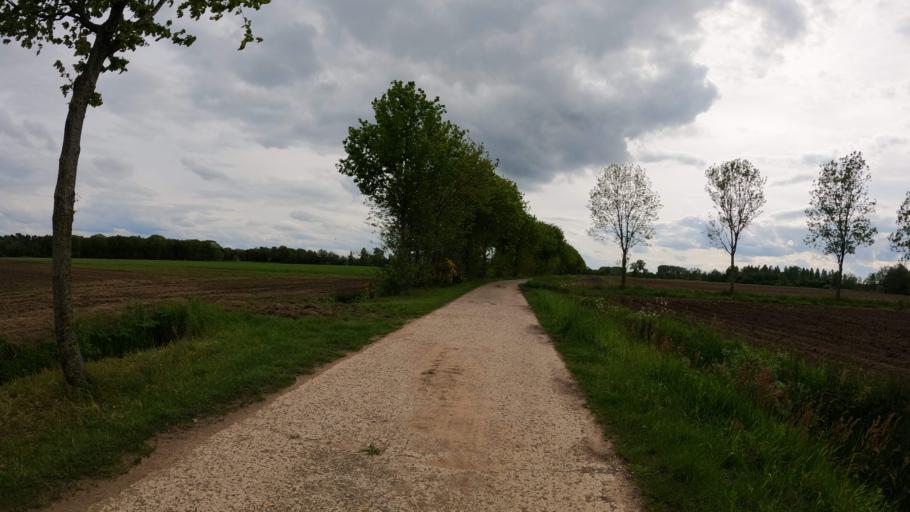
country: BE
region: Flanders
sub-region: Provincie Antwerpen
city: Vosselaar
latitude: 51.2726
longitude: 4.8988
